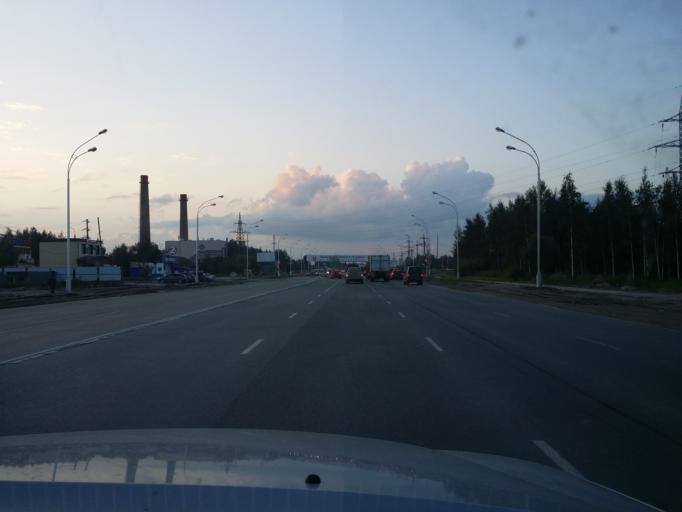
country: RU
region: Khanty-Mansiyskiy Avtonomnyy Okrug
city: Nizhnevartovsk
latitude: 60.9432
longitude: 76.5301
